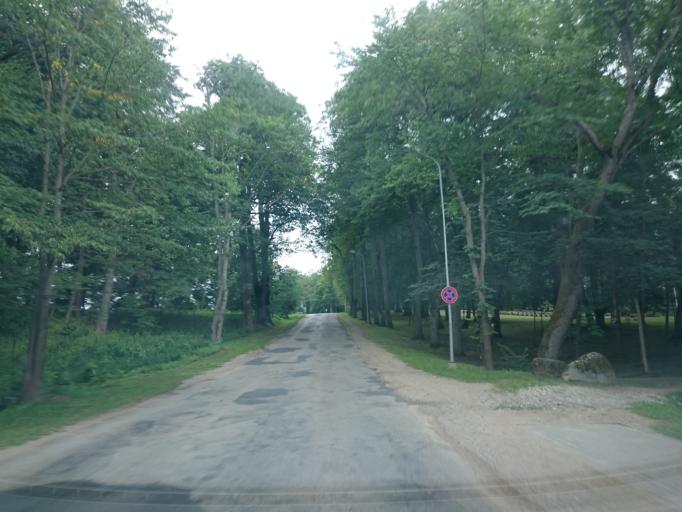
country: LV
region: Pavilostas
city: Pavilosta
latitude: 56.8805
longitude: 21.2103
